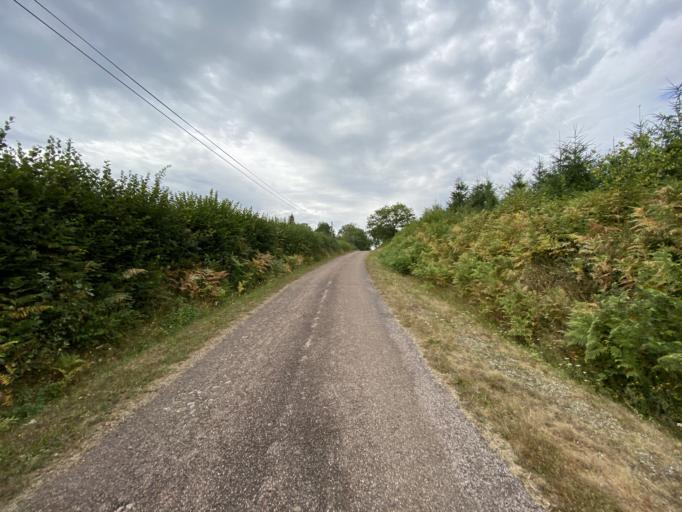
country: FR
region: Bourgogne
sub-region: Departement de la Cote-d'Or
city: Saulieu
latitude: 47.2673
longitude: 4.1486
